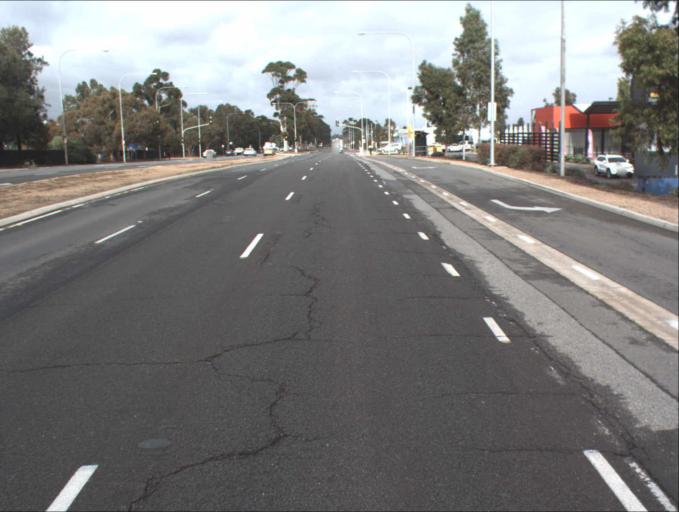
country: AU
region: South Australia
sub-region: Port Adelaide Enfield
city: Enfield
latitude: -34.8363
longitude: 138.6088
